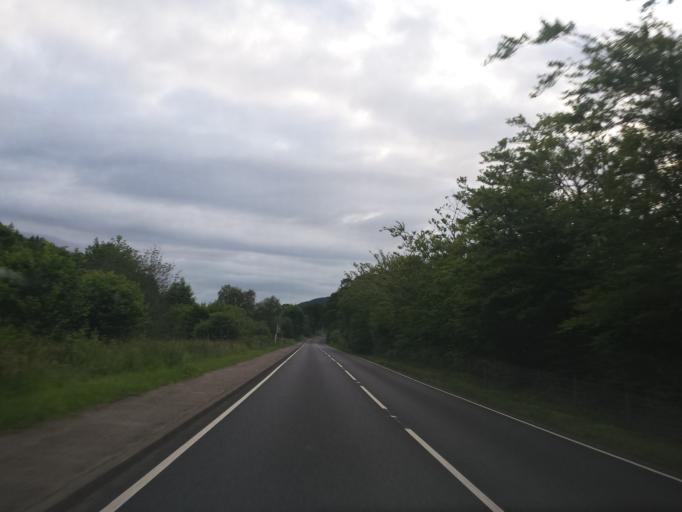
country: GB
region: Scotland
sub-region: Highland
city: Portree
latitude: 57.2850
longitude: -5.5599
